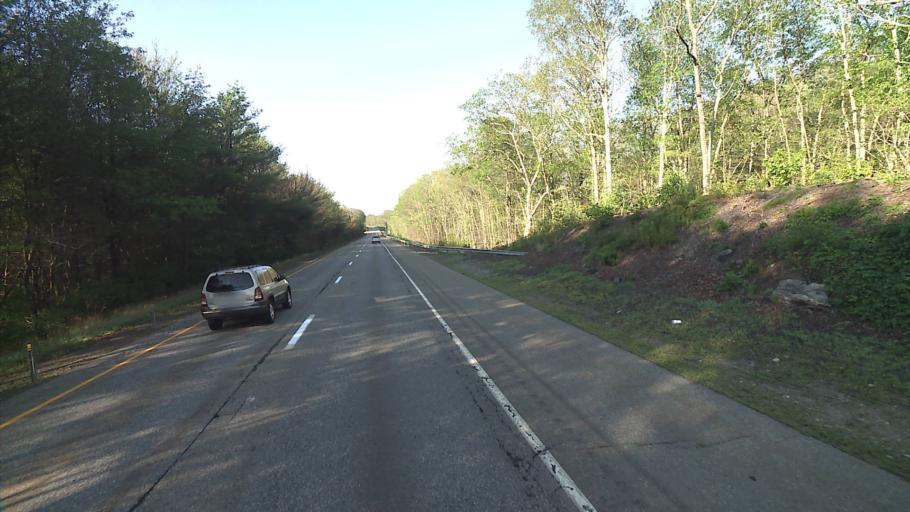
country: US
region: Connecticut
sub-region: Windham County
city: Thompson
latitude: 41.9596
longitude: -71.8768
